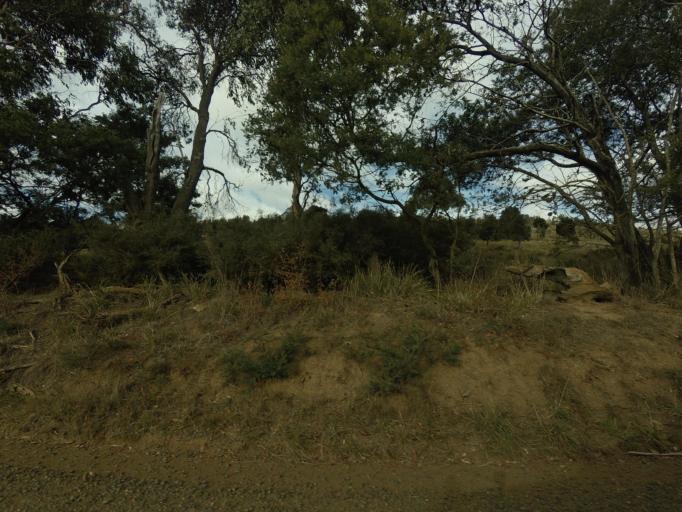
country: AU
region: Tasmania
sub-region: Brighton
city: Bridgewater
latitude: -42.4136
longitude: 147.3977
